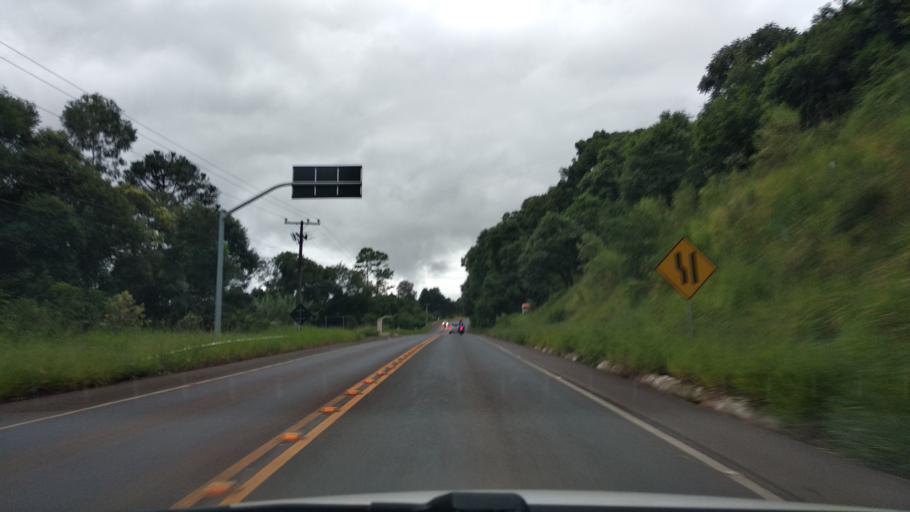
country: BR
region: Santa Catarina
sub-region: Videira
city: Videira
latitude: -27.0488
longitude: -51.2188
